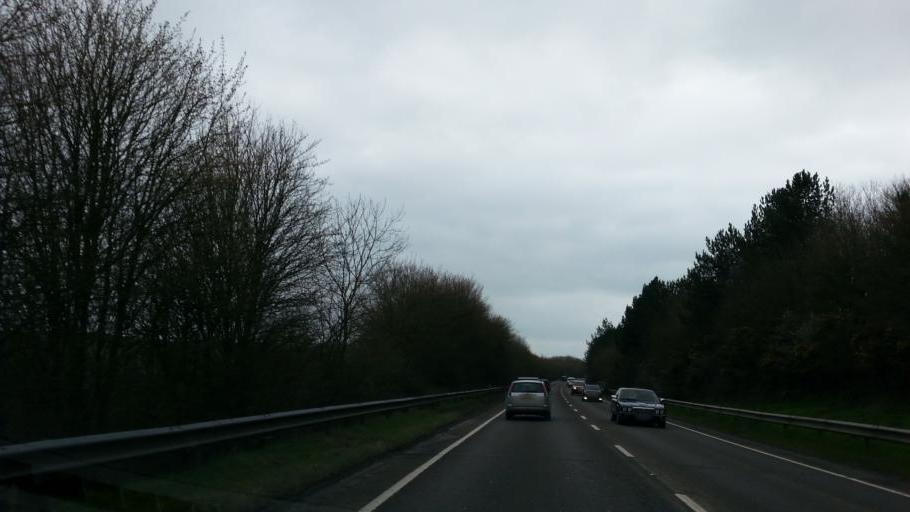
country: GB
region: England
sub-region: Devon
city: Appledore
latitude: 51.0326
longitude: -4.1715
